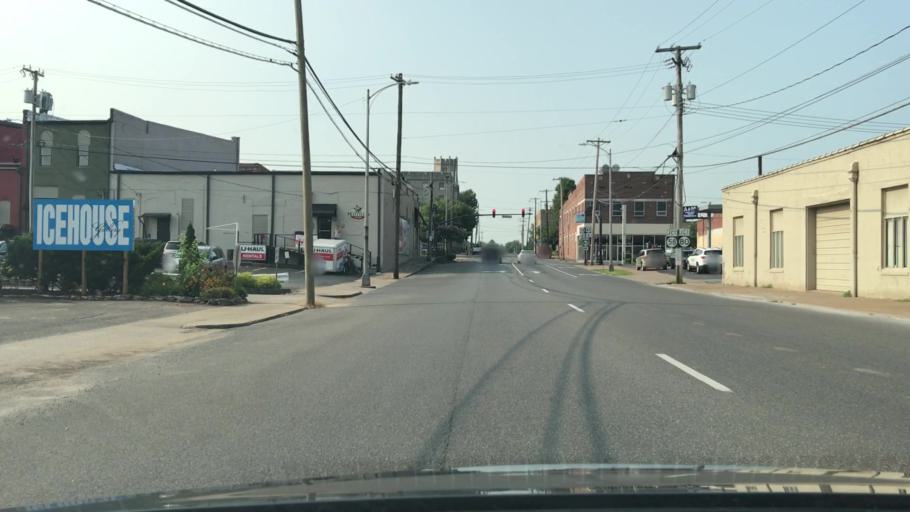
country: US
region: Kentucky
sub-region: Graves County
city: Mayfield
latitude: 36.7425
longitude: -88.6371
